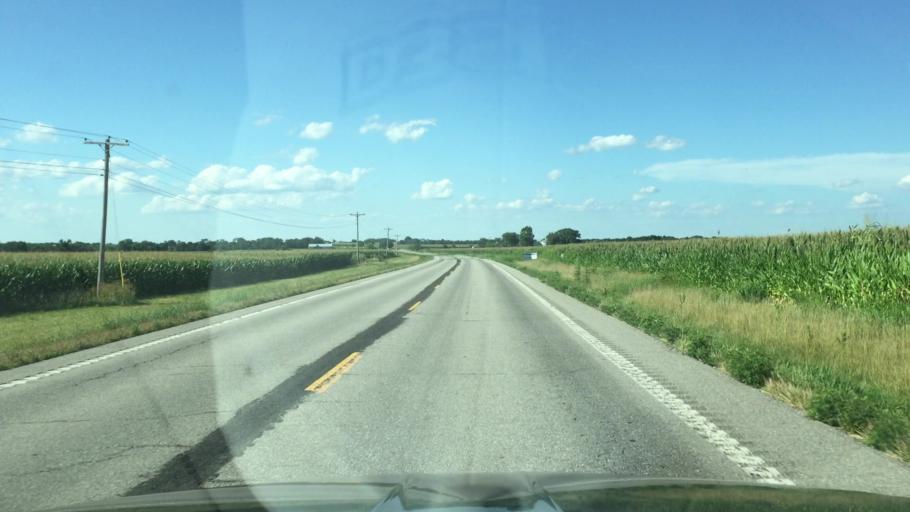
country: US
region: Missouri
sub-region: Moniteau County
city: Tipton
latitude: 38.5828
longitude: -92.7904
